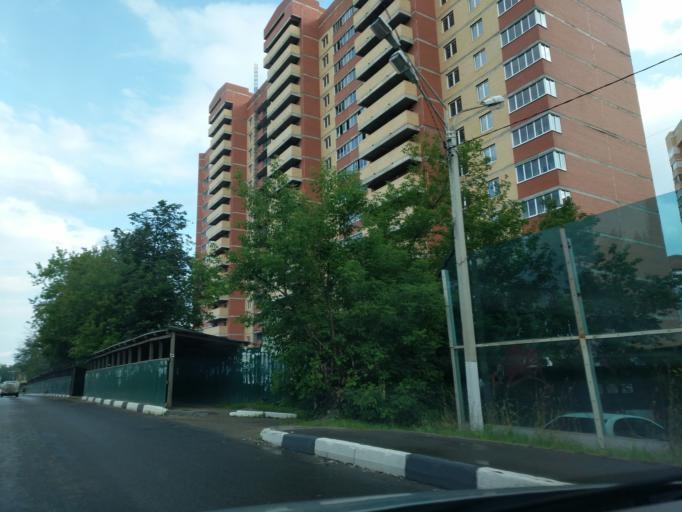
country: RU
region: Moskovskaya
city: Lobnya
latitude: 56.0222
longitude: 37.4816
